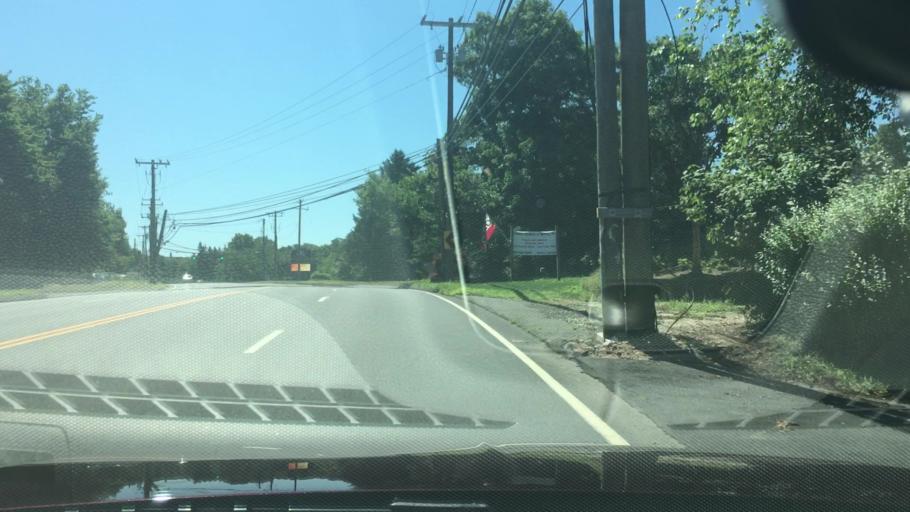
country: US
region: Connecticut
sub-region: Hartford County
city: Bristol
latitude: 41.6547
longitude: -72.9128
